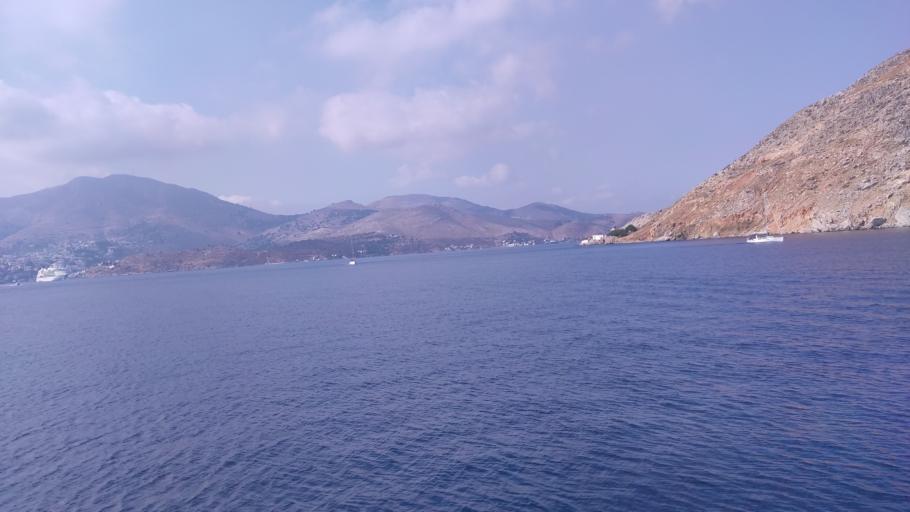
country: GR
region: South Aegean
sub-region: Nomos Dodekanisou
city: Symi
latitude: 36.6433
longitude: 27.8421
